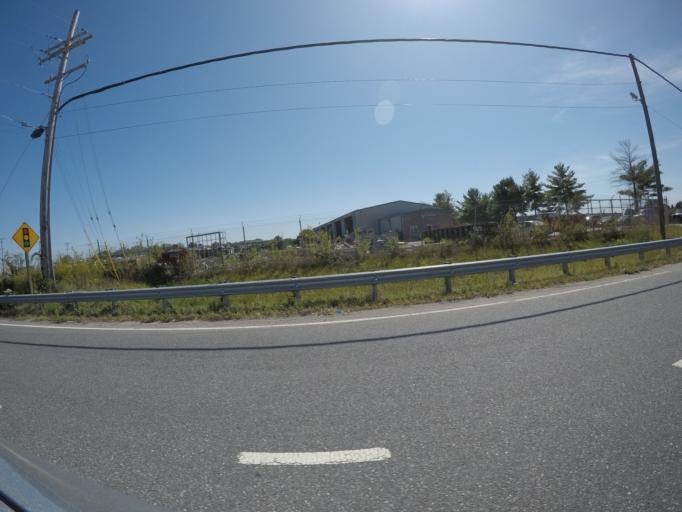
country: US
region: Maryland
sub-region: Harford County
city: Aberdeen
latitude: 39.4917
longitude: -76.1809
